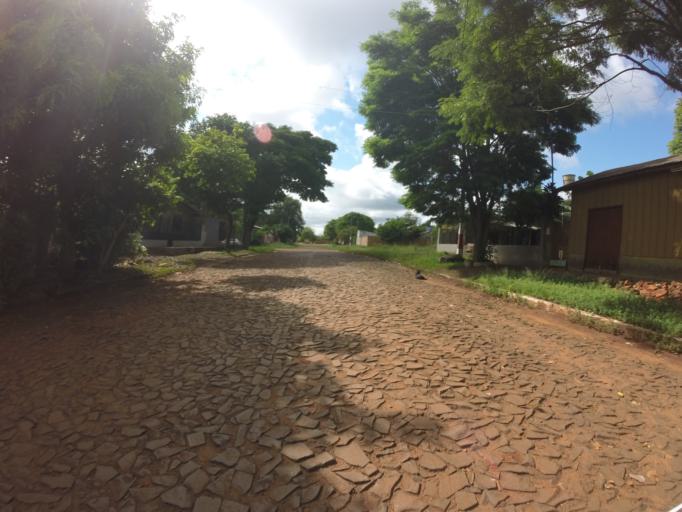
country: PY
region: Alto Parana
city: Ciudad del Este
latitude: -25.4007
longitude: -54.6468
